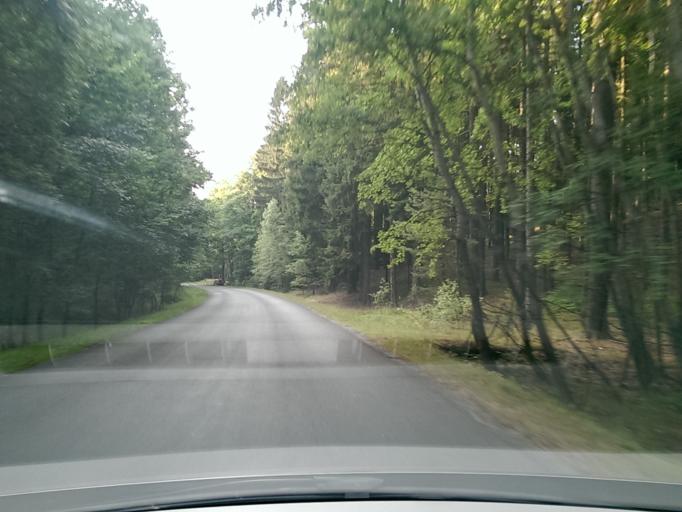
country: CZ
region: Central Bohemia
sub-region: Okres Mlada Boleslav
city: Zd'ar
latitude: 50.5031
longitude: 15.1179
